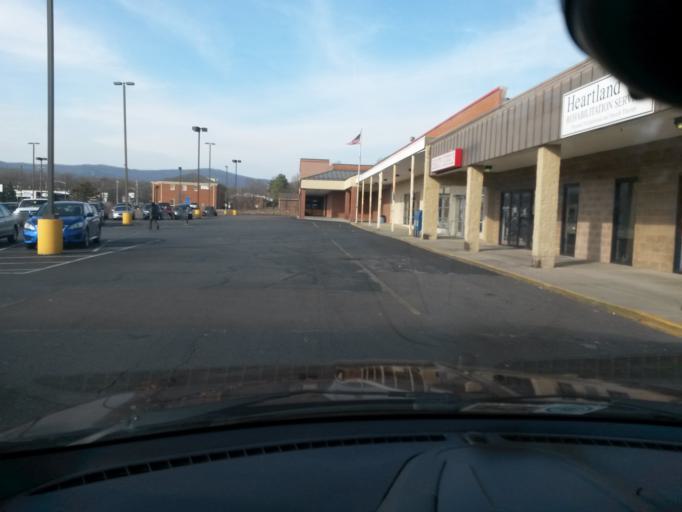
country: US
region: Virginia
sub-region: Roanoke County
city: Hollins
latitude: 37.3358
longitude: -79.9544
